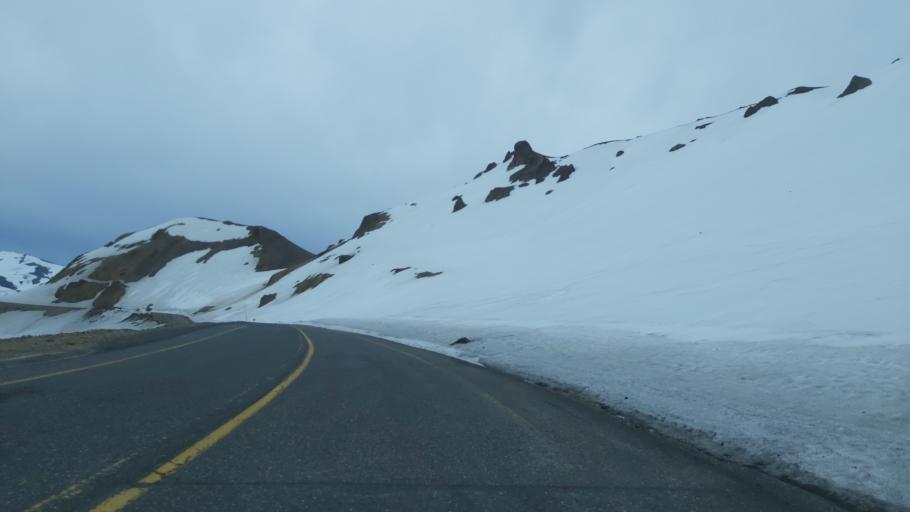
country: CL
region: Maule
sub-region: Provincia de Linares
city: Colbun
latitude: -36.0131
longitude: -70.5098
